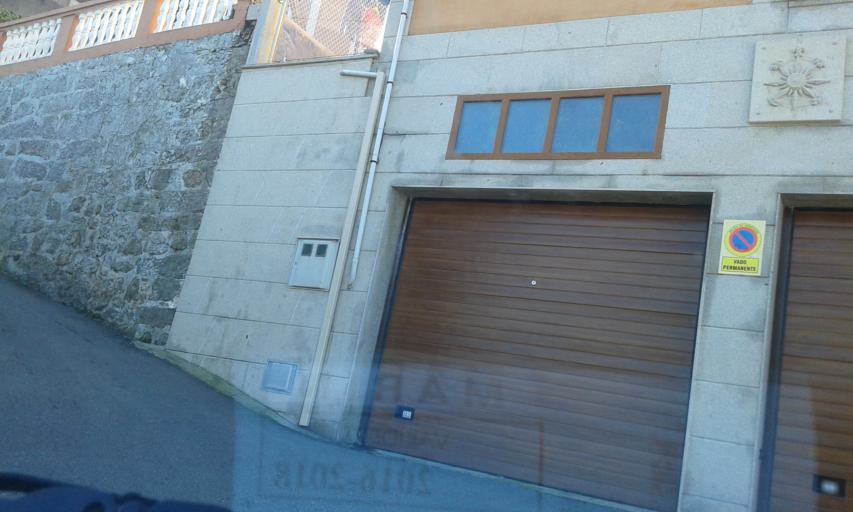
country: ES
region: Galicia
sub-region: Provincia de Pontevedra
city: Marin
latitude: 42.3669
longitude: -8.7415
